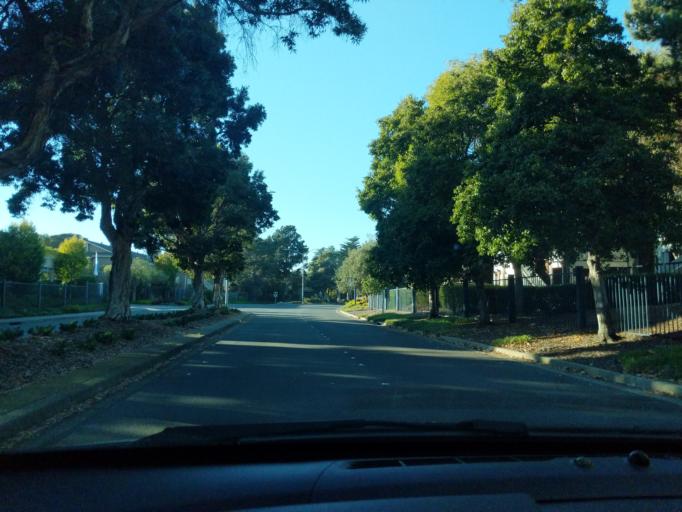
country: US
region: California
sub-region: Contra Costa County
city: Richmond
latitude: 37.9119
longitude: -122.3427
